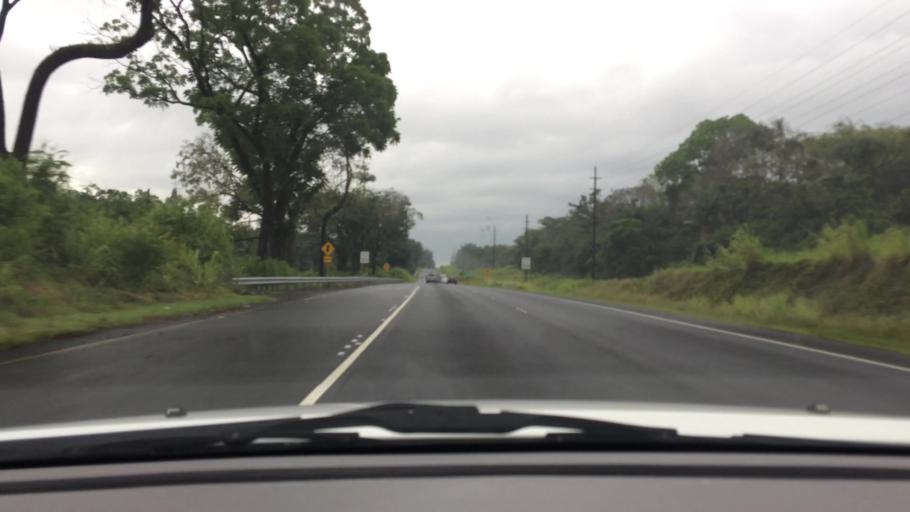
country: US
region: Hawaii
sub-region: Hawaii County
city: Kea'au
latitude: 19.6492
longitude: -155.0510
